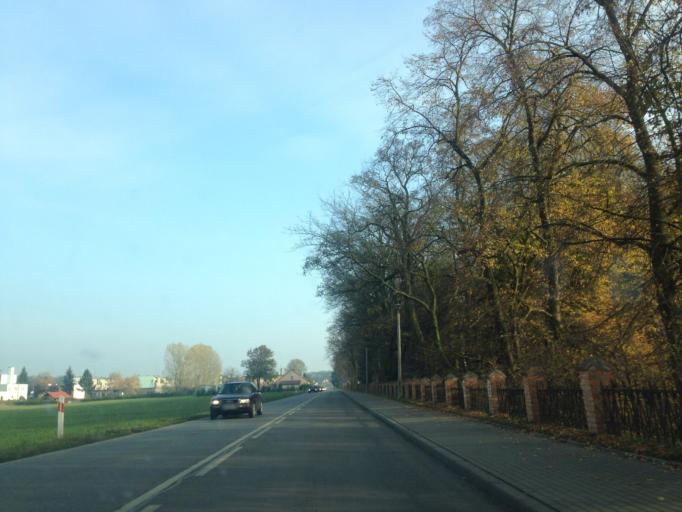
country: PL
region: Kujawsko-Pomorskie
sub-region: Powiat wabrzeski
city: Wabrzezno
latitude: 53.2662
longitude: 18.9893
